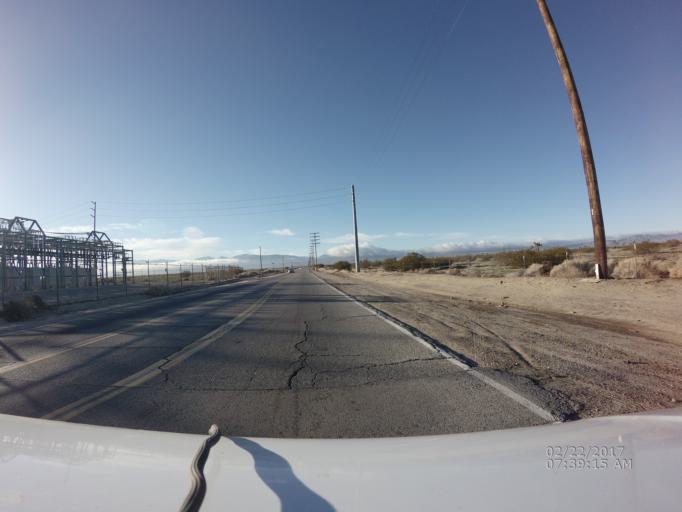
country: US
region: California
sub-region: Los Angeles County
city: Littlerock
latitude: 34.6165
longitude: -117.9696
